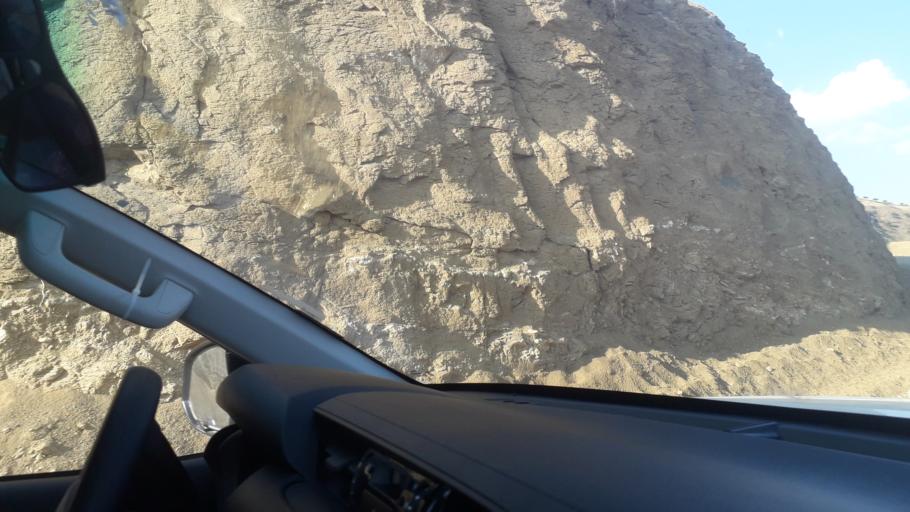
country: ET
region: Amhara
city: Dese
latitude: 11.5176
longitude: 39.2514
